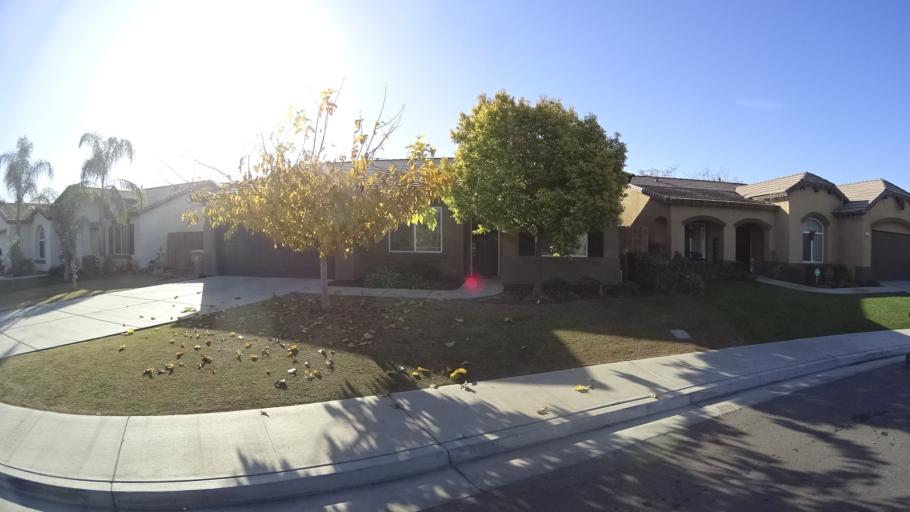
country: US
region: California
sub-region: Kern County
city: Greenfield
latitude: 35.2727
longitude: -119.0293
